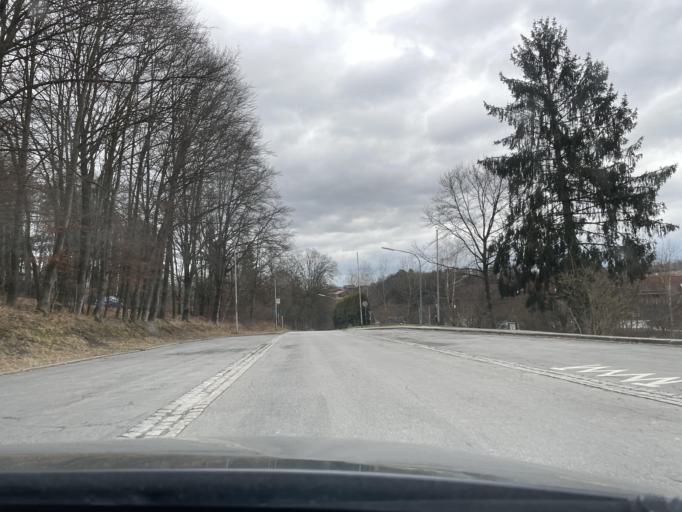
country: DE
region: Bavaria
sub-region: Lower Bavaria
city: Viechtach
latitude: 49.0804
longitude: 12.8633
